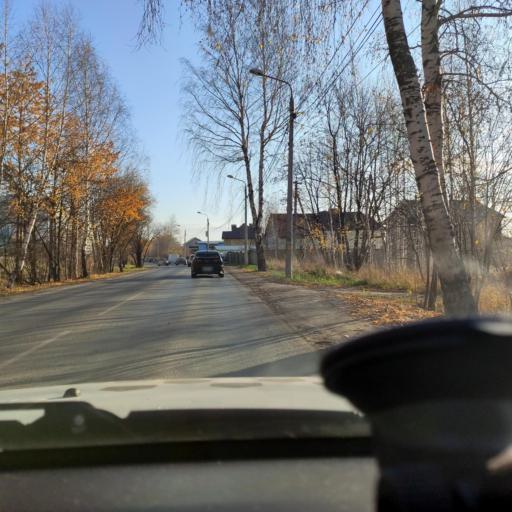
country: RU
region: Perm
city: Perm
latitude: 58.0487
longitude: 56.3421
